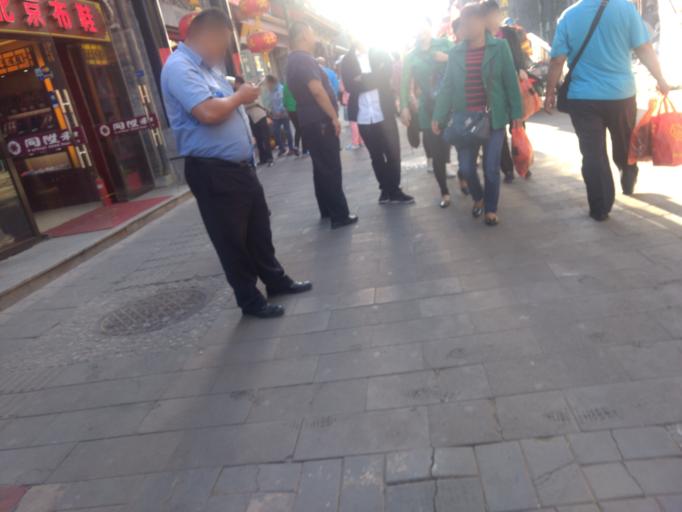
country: CN
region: Beijing
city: Beijing
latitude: 39.8946
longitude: 116.3907
